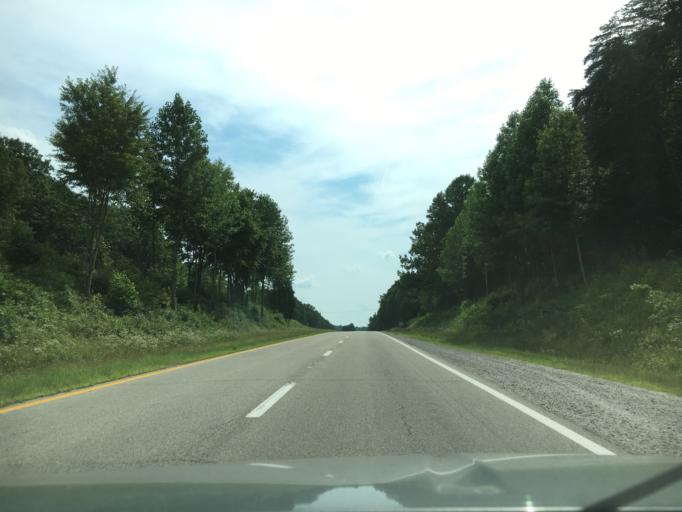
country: US
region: Virginia
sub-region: Lunenburg County
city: Victoria
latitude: 37.1196
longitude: -78.3372
